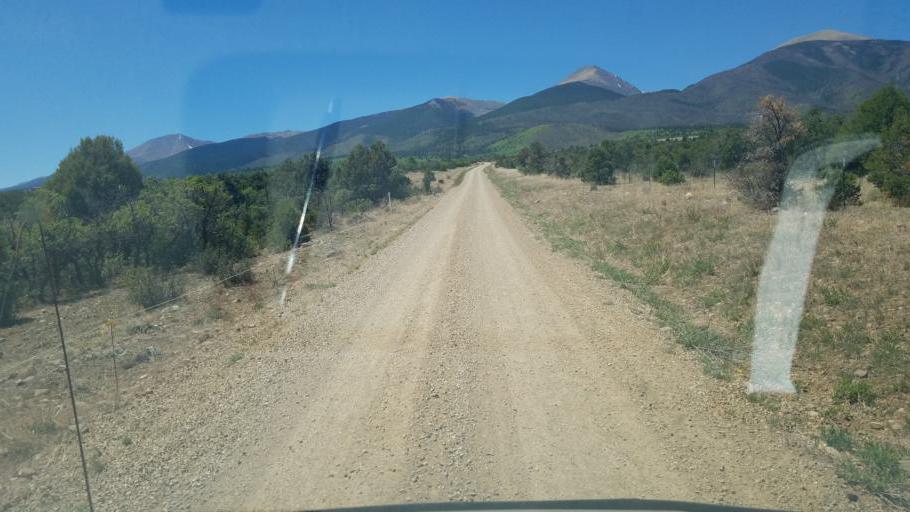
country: US
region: Colorado
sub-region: Custer County
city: Westcliffe
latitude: 38.3012
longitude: -105.6687
